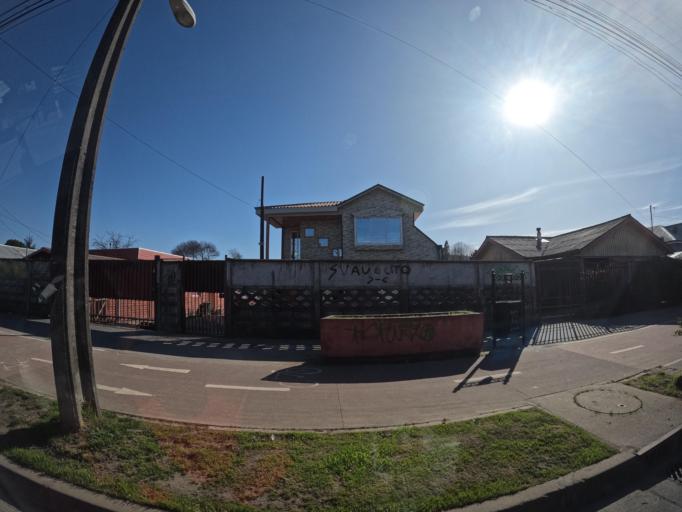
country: CL
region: Biobio
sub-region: Provincia de Concepcion
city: Chiguayante
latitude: -36.9711
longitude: -72.9365
